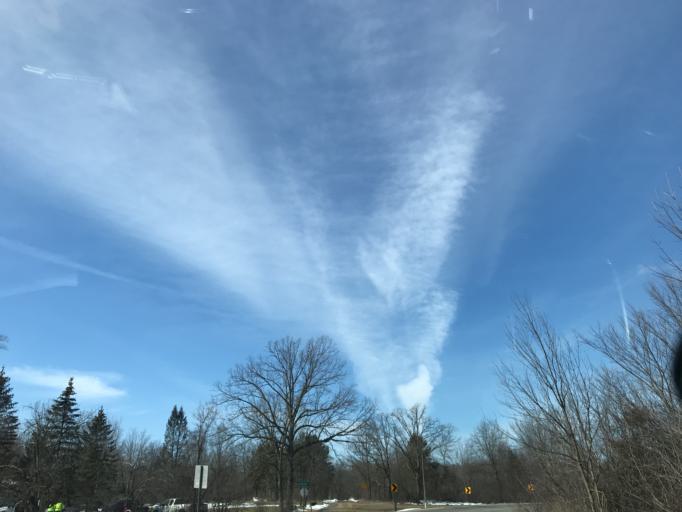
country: US
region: Michigan
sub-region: Livingston County
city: Whitmore Lake
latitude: 42.4127
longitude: -83.7370
